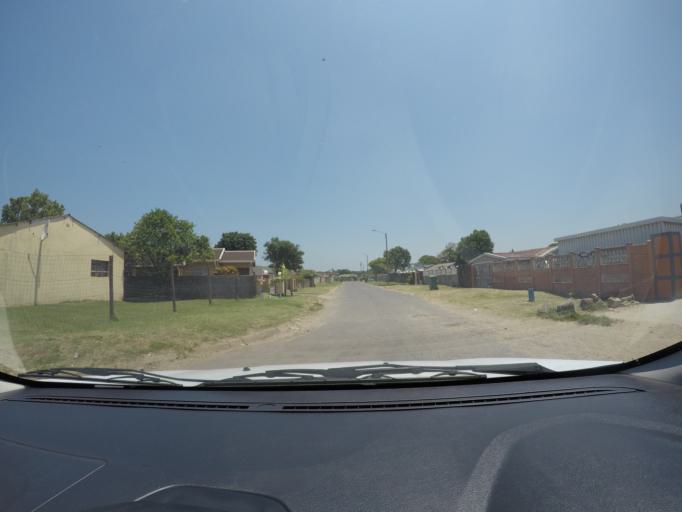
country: ZA
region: KwaZulu-Natal
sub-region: uThungulu District Municipality
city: eSikhawini
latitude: -28.8868
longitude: 31.8896
